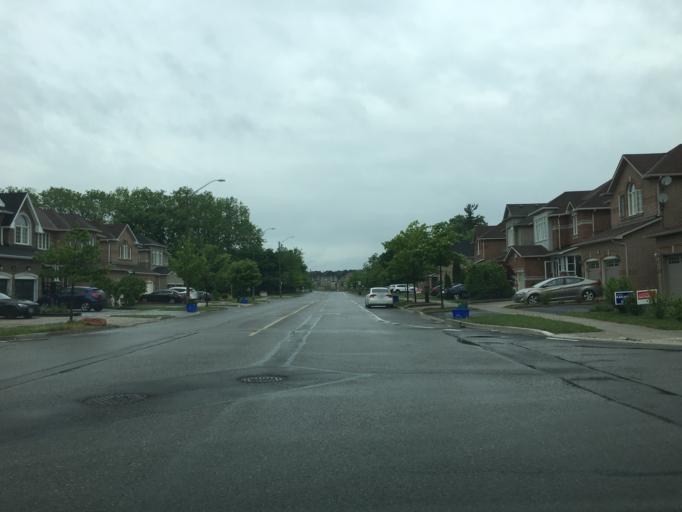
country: CA
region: Ontario
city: Markham
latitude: 43.8391
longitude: -79.2459
